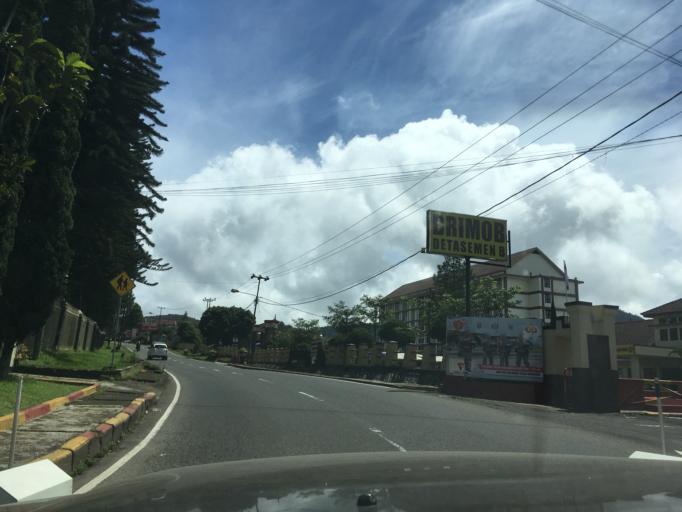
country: ID
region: West Java
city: Lembang
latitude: -6.7961
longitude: 107.6540
